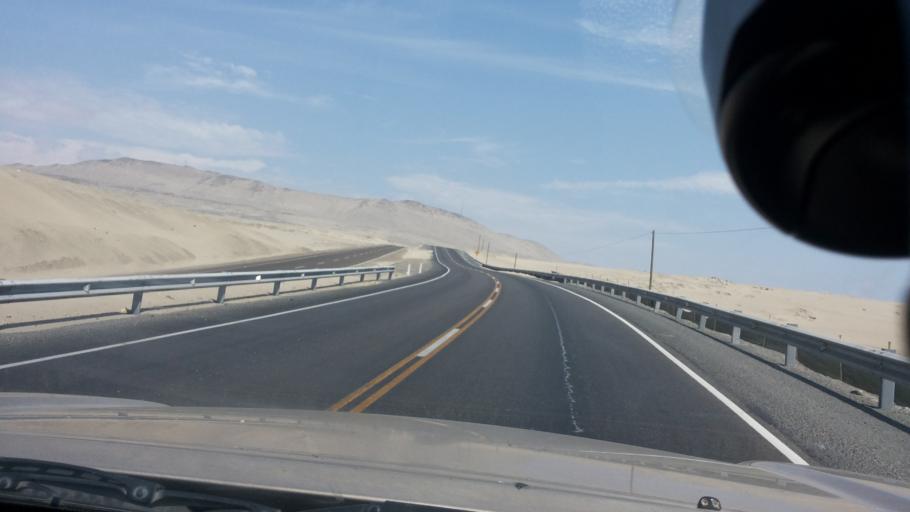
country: PE
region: Ancash
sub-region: Provincia de Huarmey
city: La Caleta Culebras
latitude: -9.7324
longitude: -78.2582
